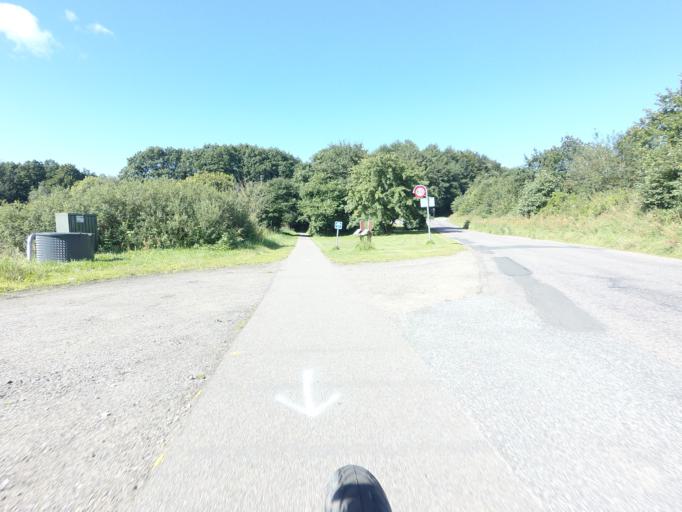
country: DK
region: Central Jutland
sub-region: Horsens Kommune
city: Braedstrup
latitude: 55.9733
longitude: 9.6276
